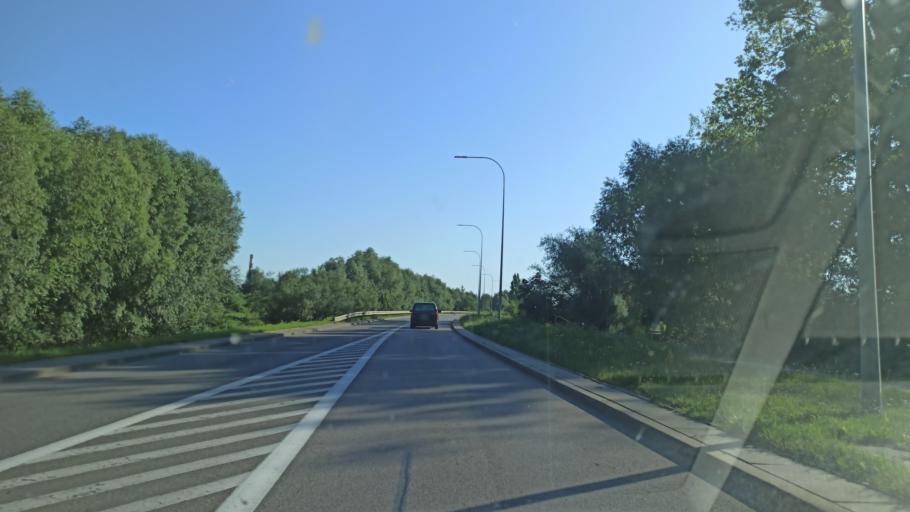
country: PL
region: Warmian-Masurian Voivodeship
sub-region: Powiat elblaski
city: Elblag
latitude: 54.1679
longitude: 19.3780
